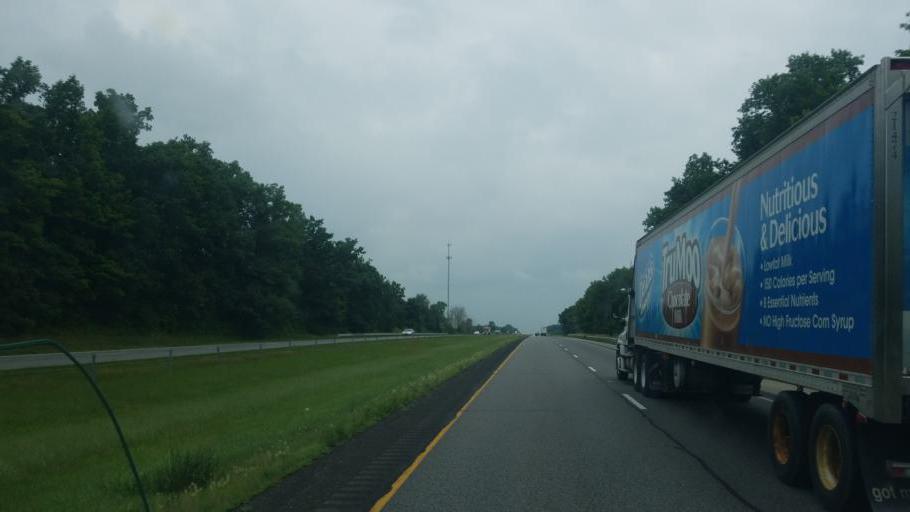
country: US
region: Indiana
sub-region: Grant County
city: Upland
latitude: 40.5026
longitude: -85.5492
